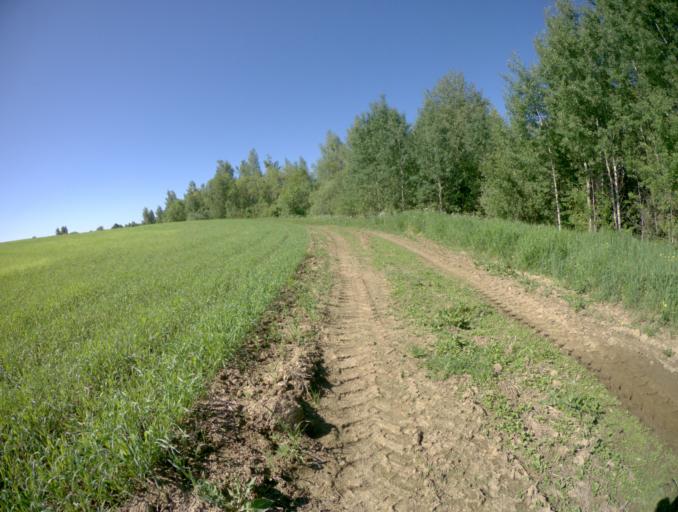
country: RU
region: Ivanovo
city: Gavrilov Posad
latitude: 56.5386
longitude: 40.1958
